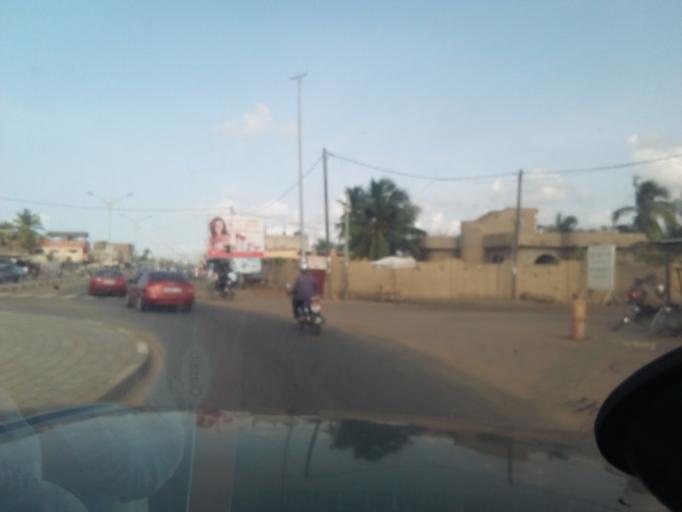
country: TG
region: Maritime
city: Lome
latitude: 6.1713
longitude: 1.3506
